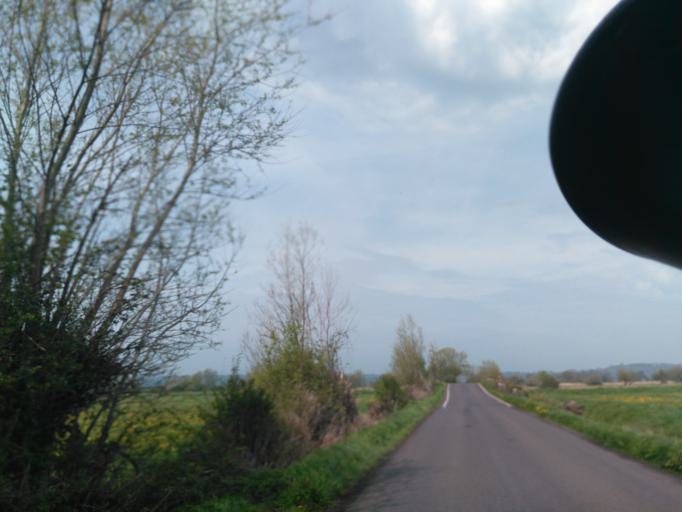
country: GB
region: England
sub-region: Somerset
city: Langport
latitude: 51.0951
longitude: -2.8204
